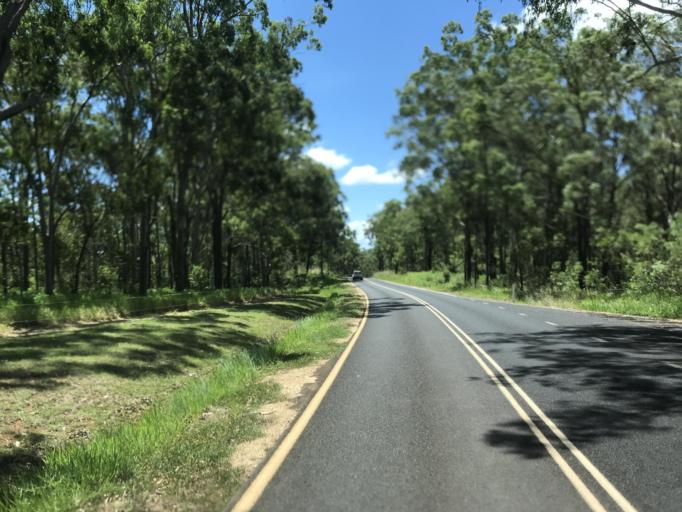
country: AU
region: Queensland
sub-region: Tablelands
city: Atherton
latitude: -17.4224
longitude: 145.3963
